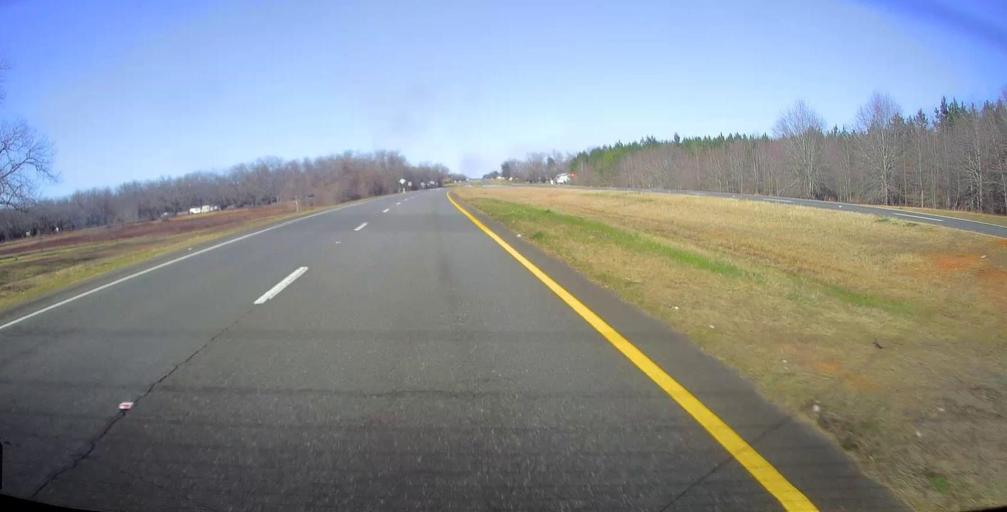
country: US
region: Georgia
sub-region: Schley County
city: Ellaville
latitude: 32.1569
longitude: -84.2706
